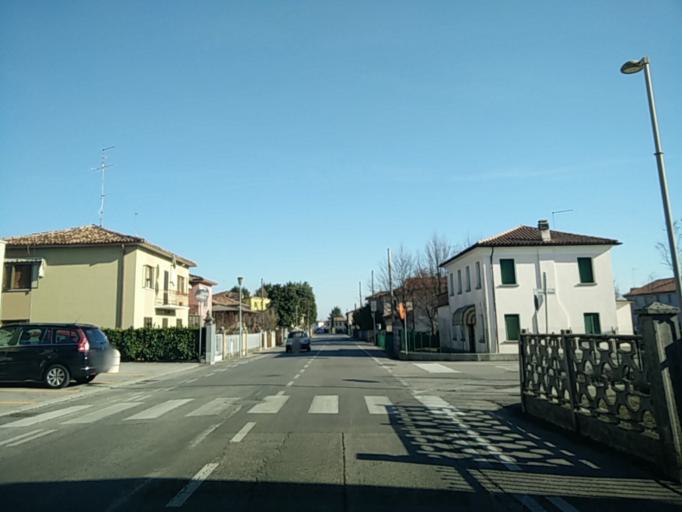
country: IT
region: Veneto
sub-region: Provincia di Treviso
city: San Vendemiano
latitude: 45.8869
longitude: 12.3466
